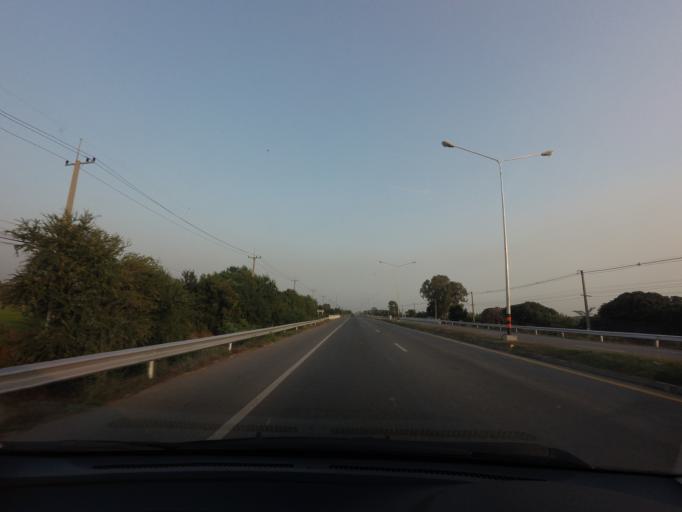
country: TH
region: Sukhothai
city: Sukhothai
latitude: 17.0202
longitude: 99.9008
